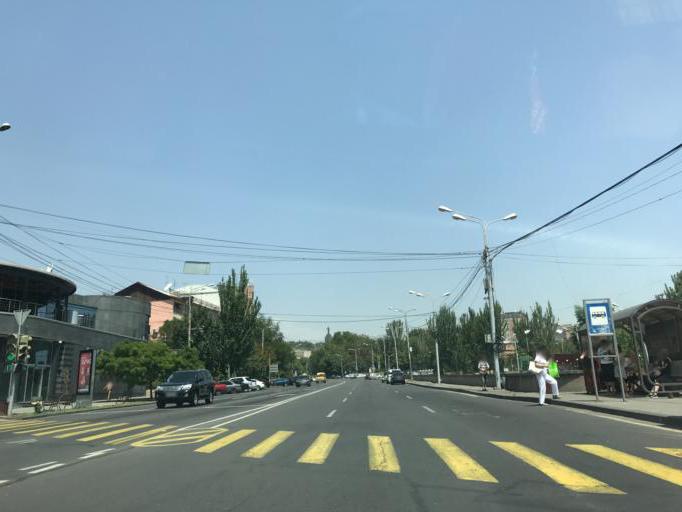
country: AM
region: Yerevan
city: Yerevan
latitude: 40.1798
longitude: 44.5236
